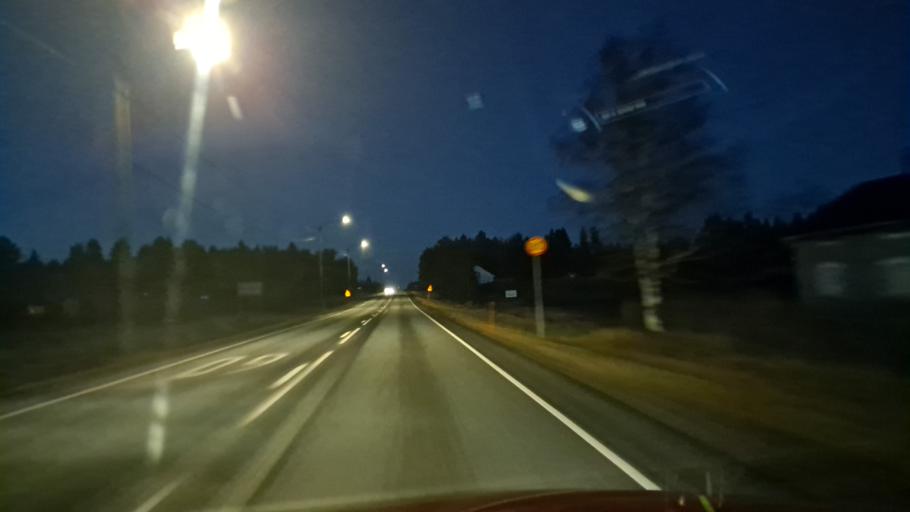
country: FI
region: Northern Ostrobothnia
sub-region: Oulunkaari
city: Ii
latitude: 65.3463
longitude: 25.3695
